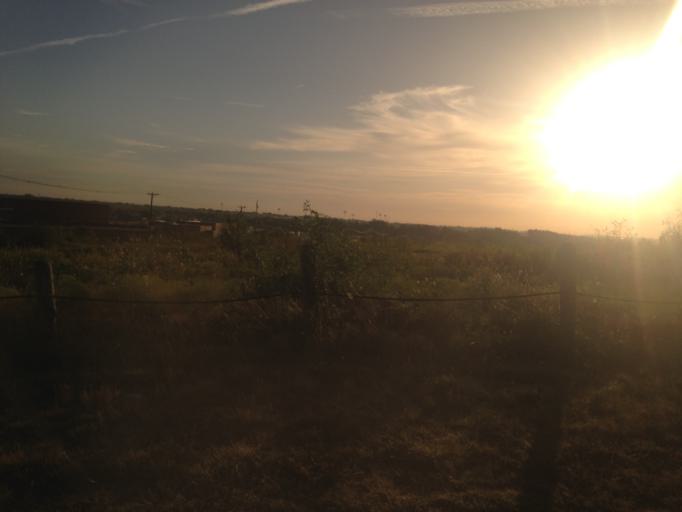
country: US
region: Texas
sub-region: Tarrant County
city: Watauga
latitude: 32.8458
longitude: -97.2817
